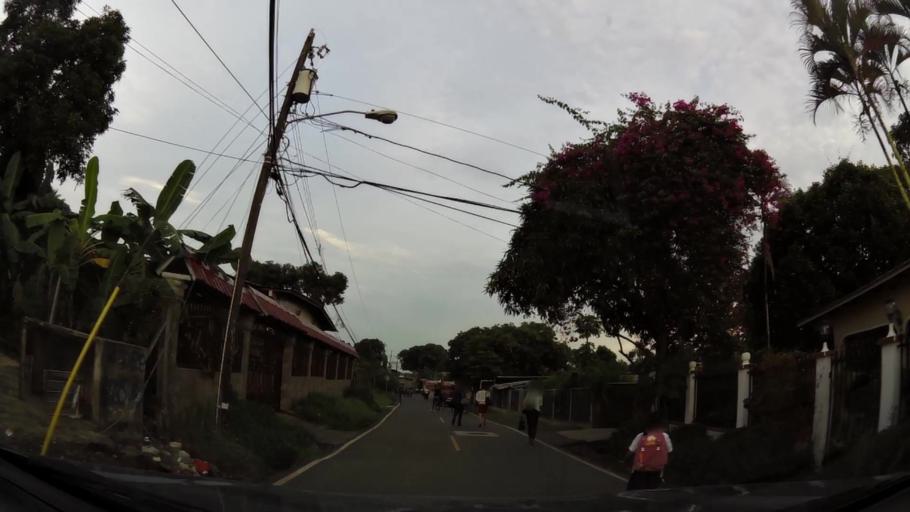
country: PA
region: Panama
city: Tocumen
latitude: 9.0808
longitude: -79.3876
